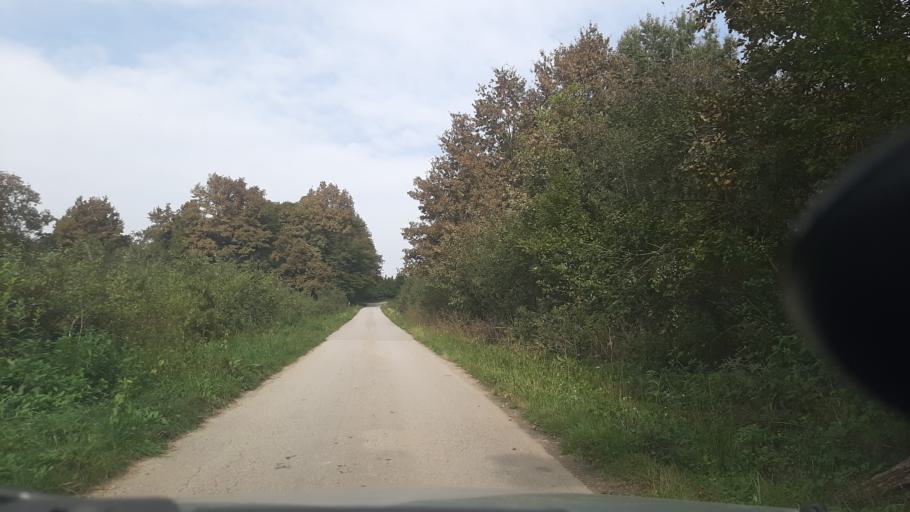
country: BA
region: Republika Srpska
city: Maglajani
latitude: 44.8710
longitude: 17.4695
